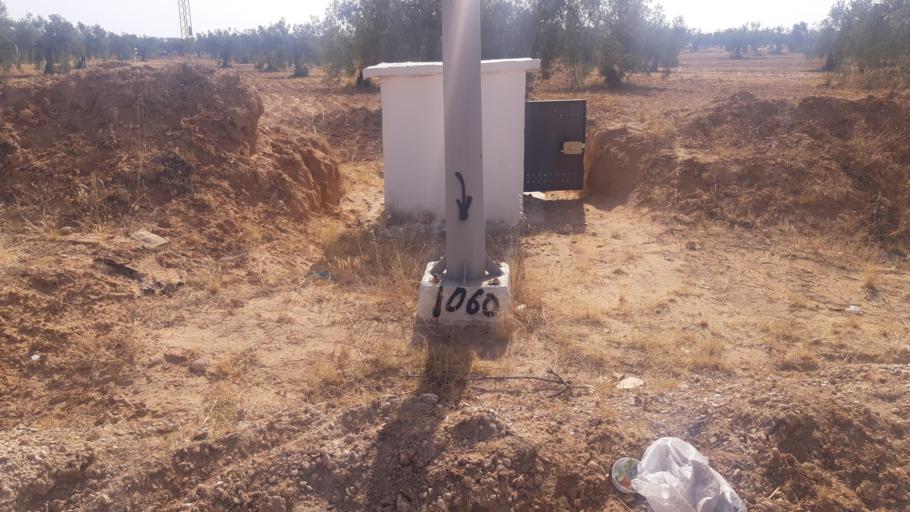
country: TN
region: Al Mahdiyah
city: El Jem
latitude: 35.1822
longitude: 10.7232
